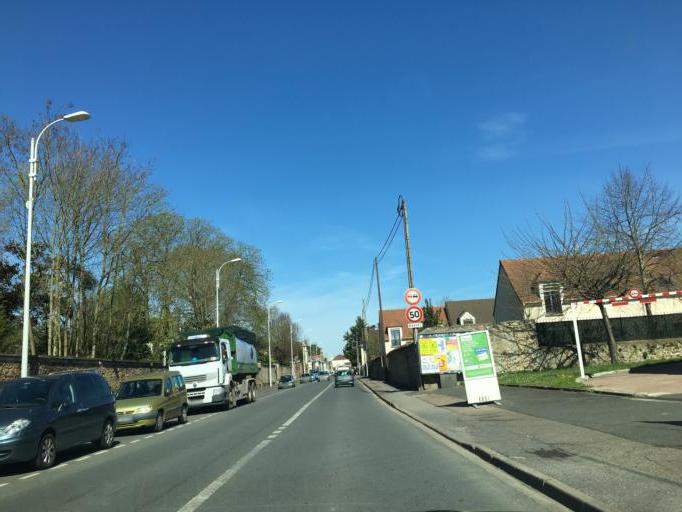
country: FR
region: Ile-de-France
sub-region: Departement de l'Essonne
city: Draveil
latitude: 48.6764
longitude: 2.4111
